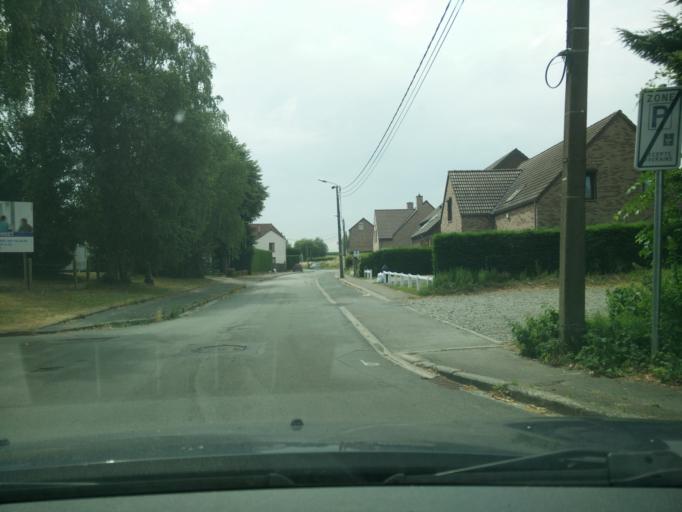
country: BE
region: Wallonia
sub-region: Province du Hainaut
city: Braine-le-Comte
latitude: 50.6047
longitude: 4.1440
